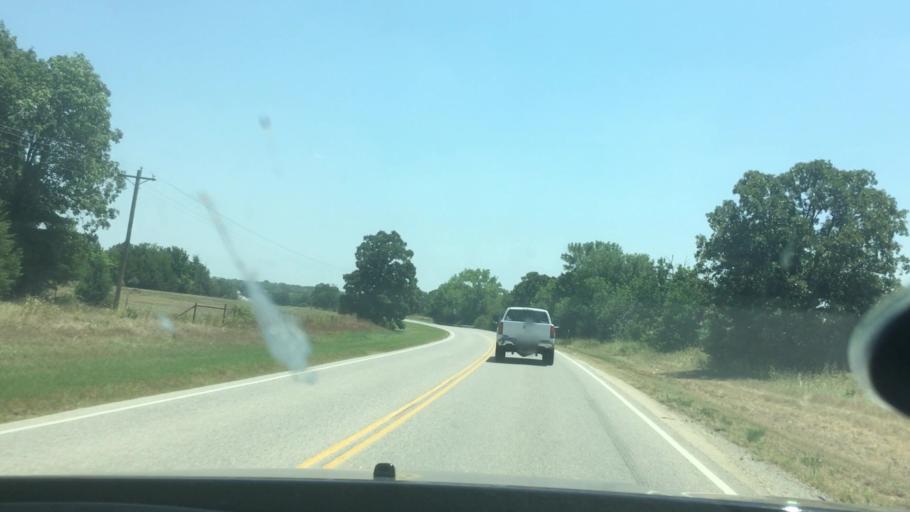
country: US
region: Oklahoma
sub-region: Bryan County
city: Durant
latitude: 34.1757
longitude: -96.4151
